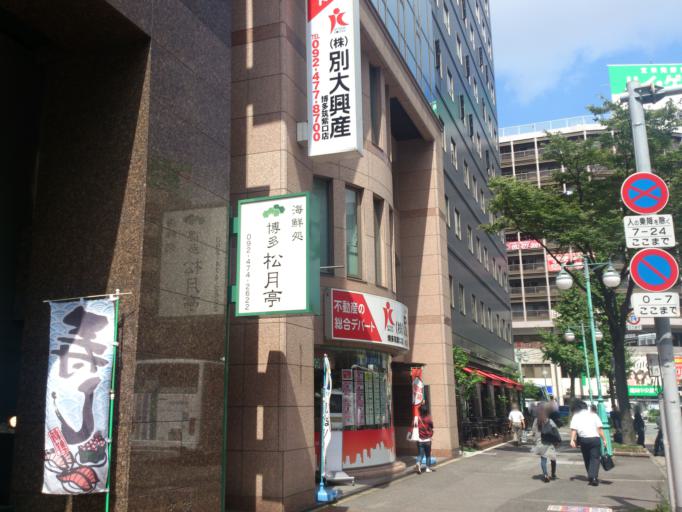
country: JP
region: Fukuoka
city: Fukuoka-shi
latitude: 33.5913
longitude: 130.4224
